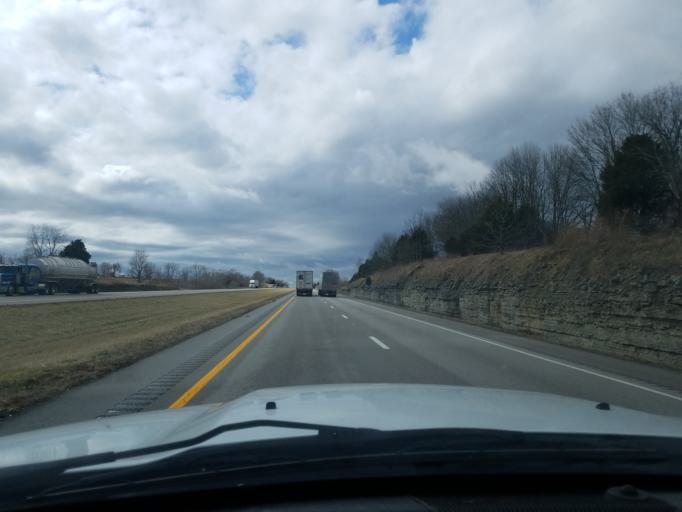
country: US
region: Kentucky
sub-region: Montgomery County
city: Mount Sterling
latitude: 38.0960
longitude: -83.8637
